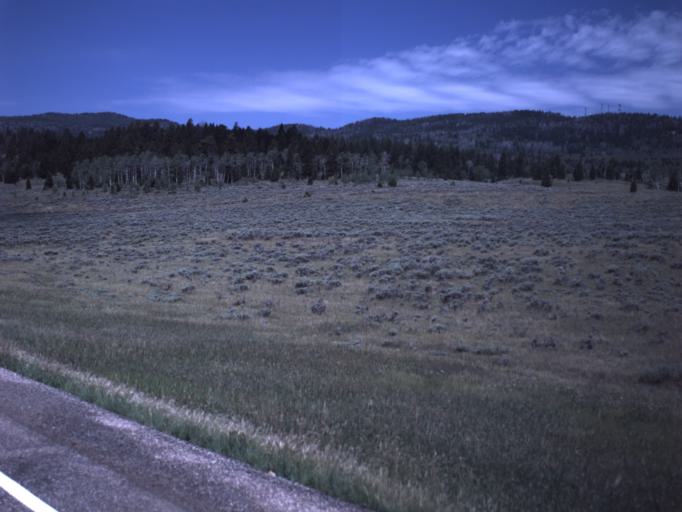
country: US
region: Utah
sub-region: Uintah County
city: Maeser
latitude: 40.7150
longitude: -109.4825
